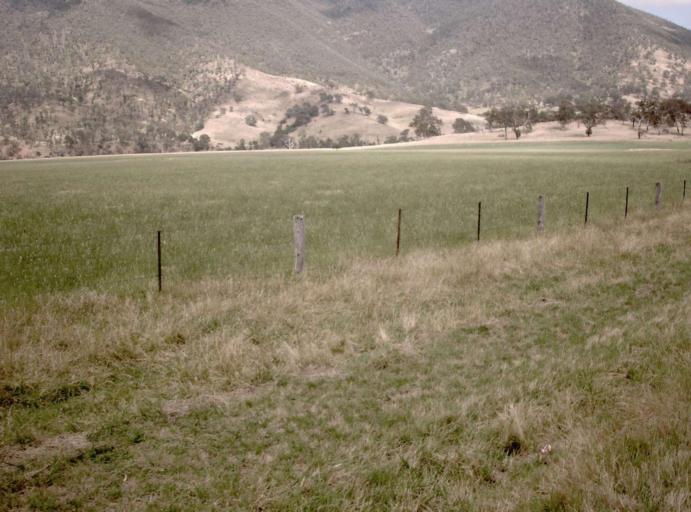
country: AU
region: Victoria
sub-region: Wellington
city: Heyfield
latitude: -37.6372
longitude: 146.6315
